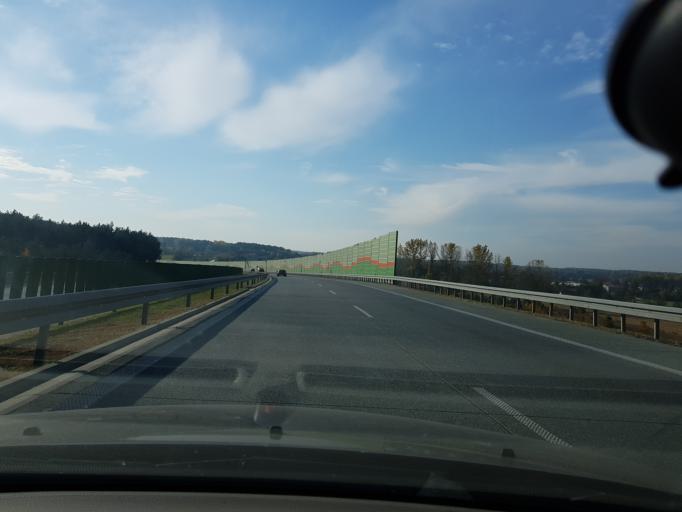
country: PL
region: Lodz Voivodeship
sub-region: Powiat rawski
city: Rawa Mazowiecka
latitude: 51.7149
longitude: 20.2197
